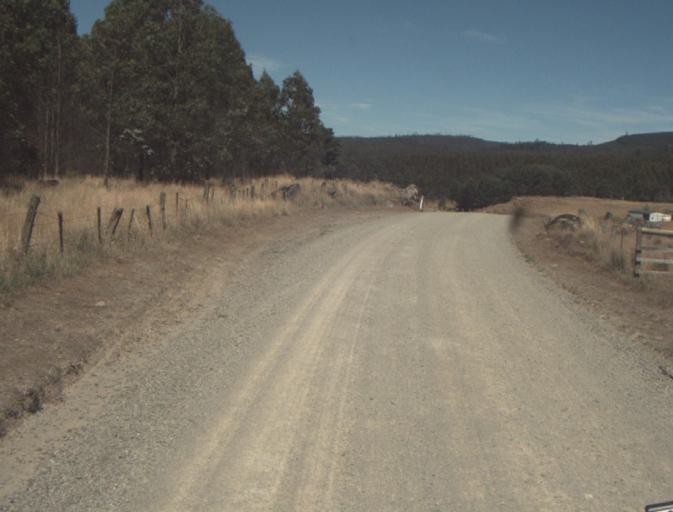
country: AU
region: Tasmania
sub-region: Dorset
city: Scottsdale
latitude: -41.3493
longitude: 147.4491
